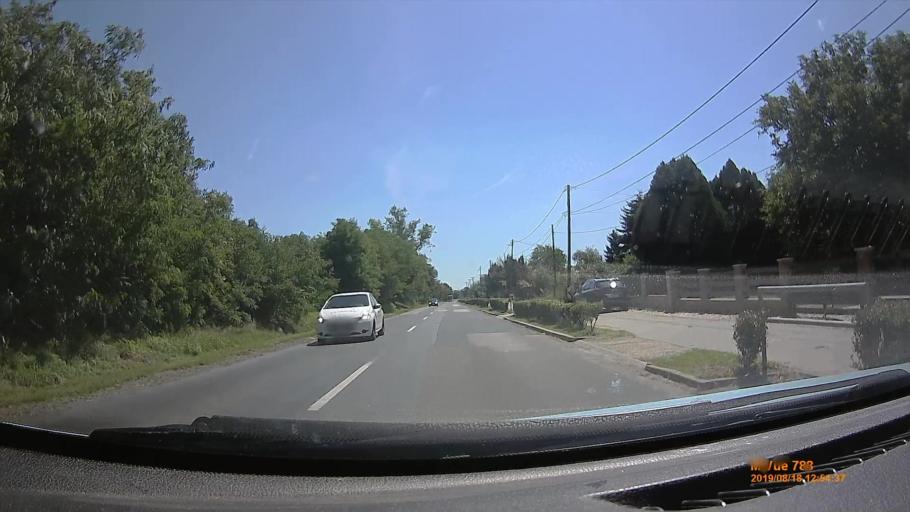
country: HU
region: Fejer
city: Aba
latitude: 47.0401
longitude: 18.5326
